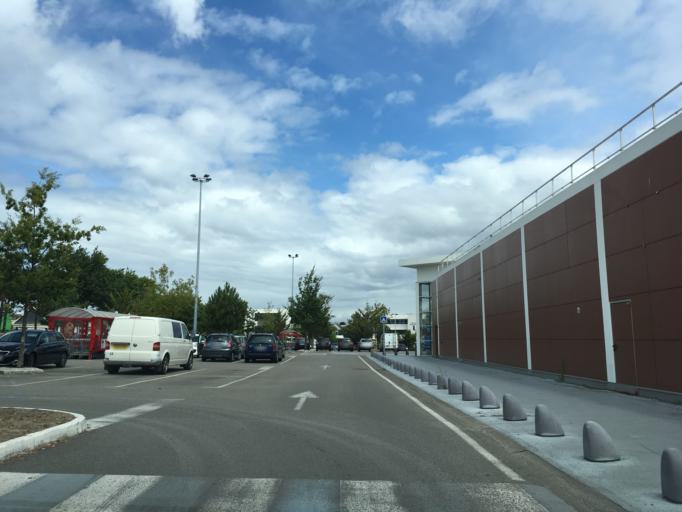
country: FR
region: Brittany
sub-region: Departement du Morbihan
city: Lorient
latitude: 47.7343
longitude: -3.3837
